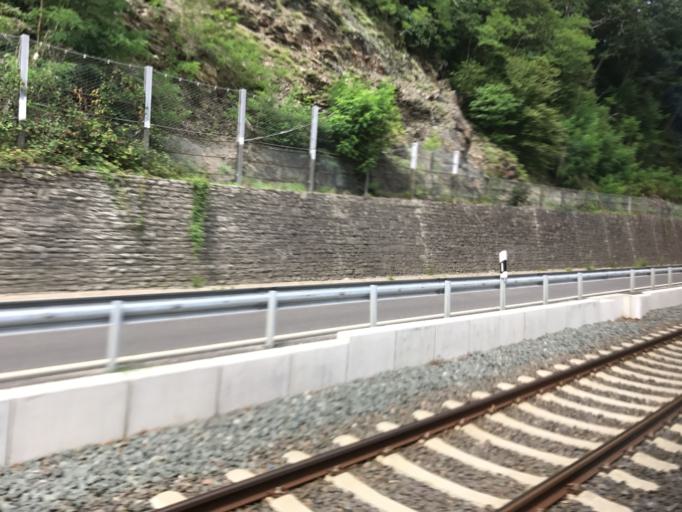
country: DE
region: Rheinland-Pfalz
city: Obernhof
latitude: 50.3100
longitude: 7.8325
